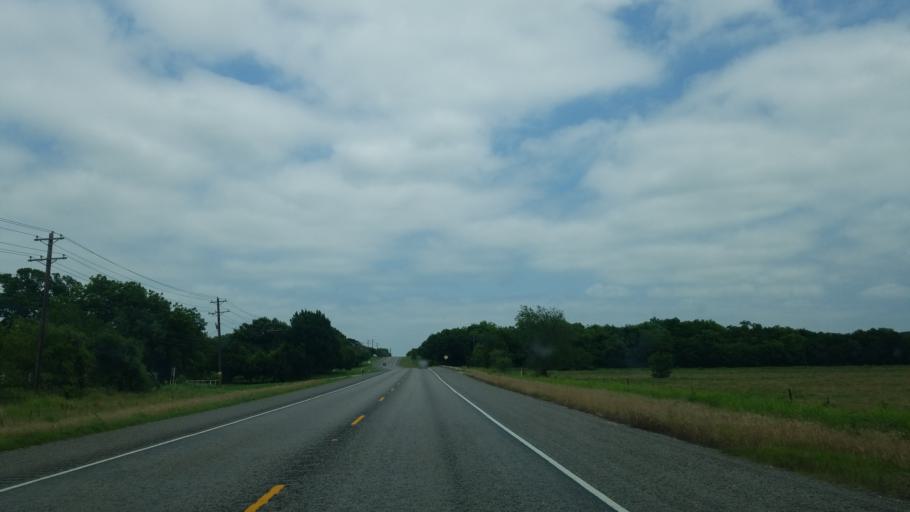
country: US
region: Texas
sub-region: Denton County
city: Aubrey
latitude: 33.3056
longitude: -97.0313
